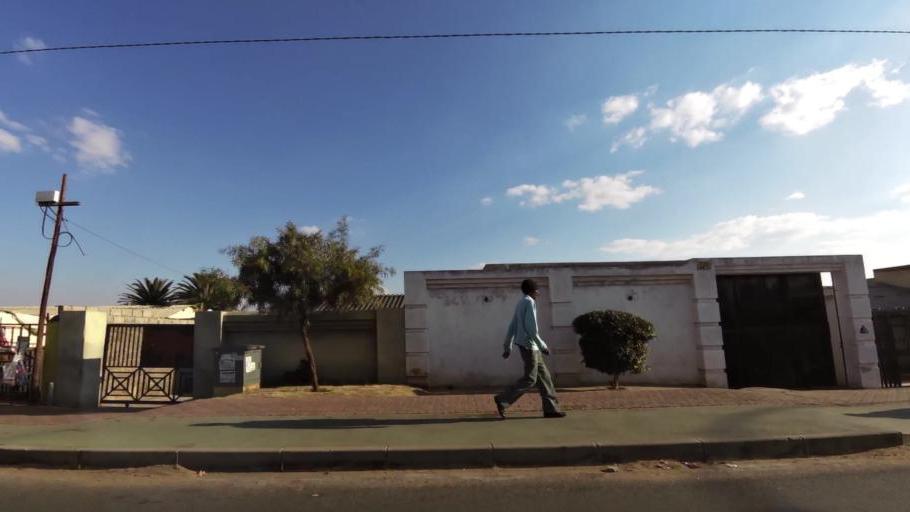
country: ZA
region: Gauteng
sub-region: City of Johannesburg Metropolitan Municipality
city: Soweto
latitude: -26.2195
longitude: 27.8871
